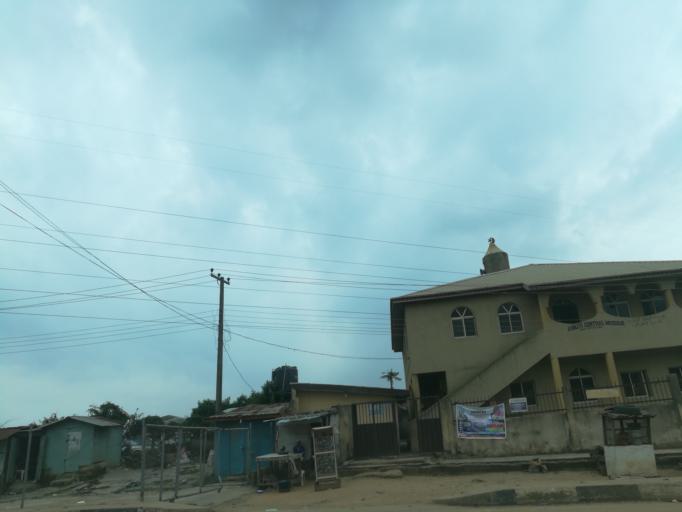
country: NG
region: Lagos
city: Ojota
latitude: 6.6169
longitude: 3.3973
